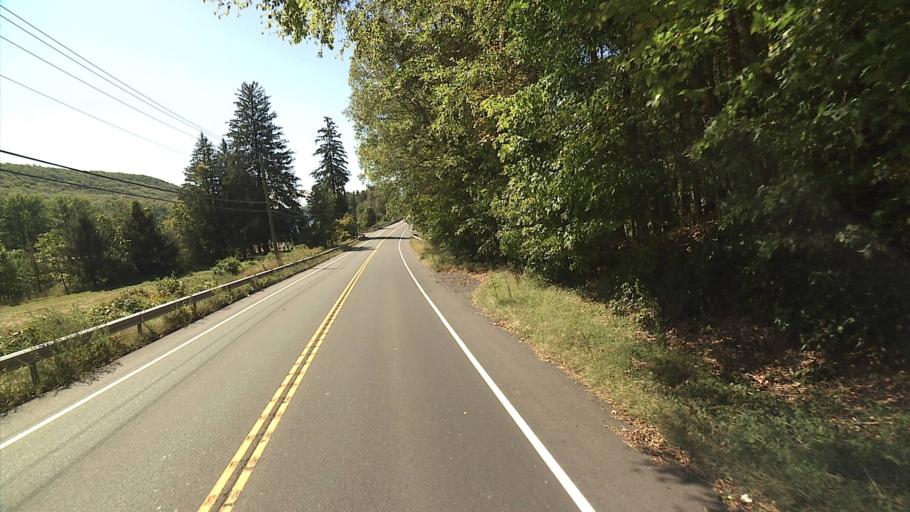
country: US
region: Connecticut
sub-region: New Haven County
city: Woodbridge
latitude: 41.3789
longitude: -72.9759
